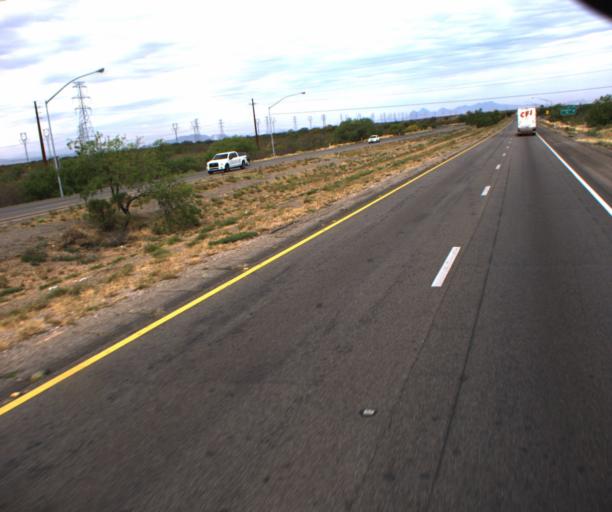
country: US
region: Arizona
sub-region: Pima County
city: Vail
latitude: 32.0582
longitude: -110.7680
